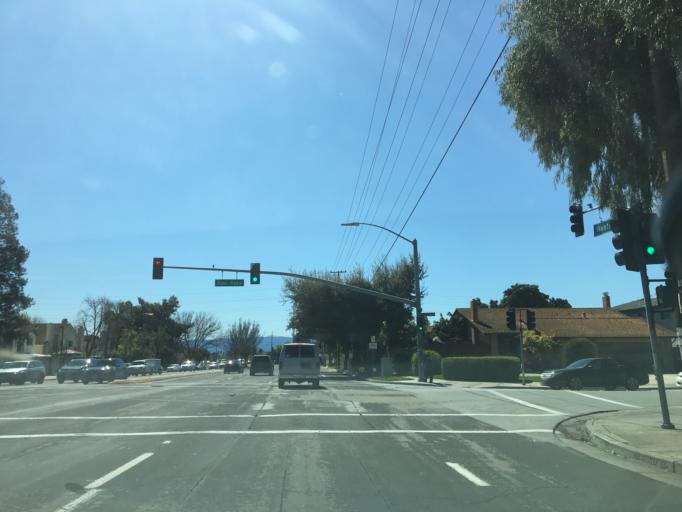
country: US
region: California
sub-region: Santa Clara County
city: Milpitas
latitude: 37.3940
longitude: -121.8759
